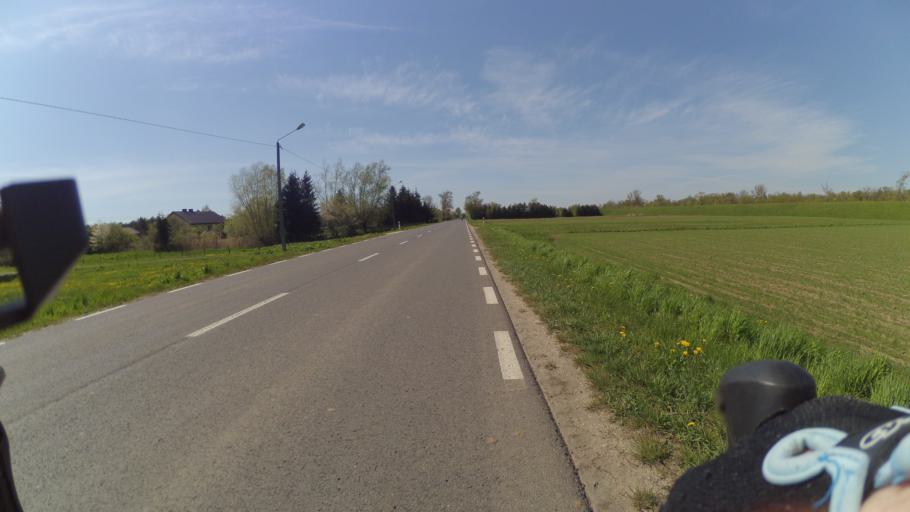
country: PL
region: Masovian Voivodeship
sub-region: Powiat plonski
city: Czerwinsk Nad Wisla
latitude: 52.3777
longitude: 20.3418
